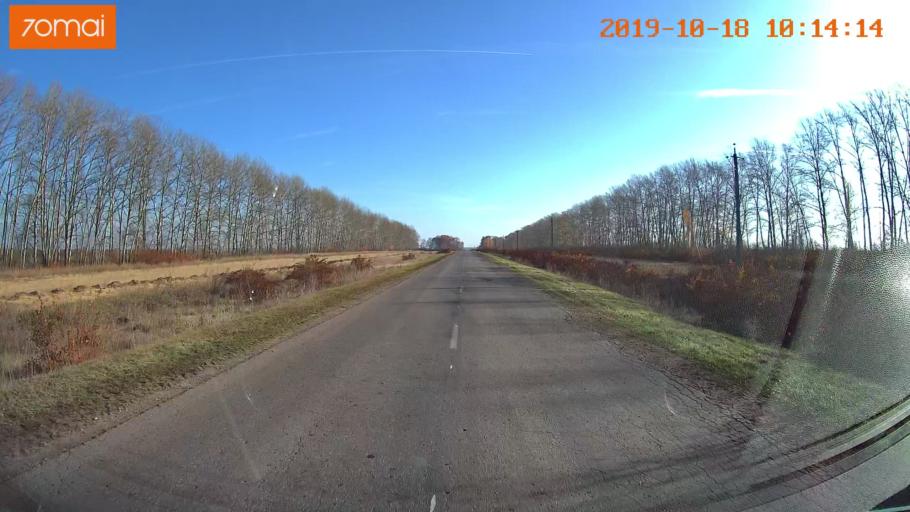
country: RU
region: Tula
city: Kurkino
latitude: 53.4042
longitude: 38.5376
